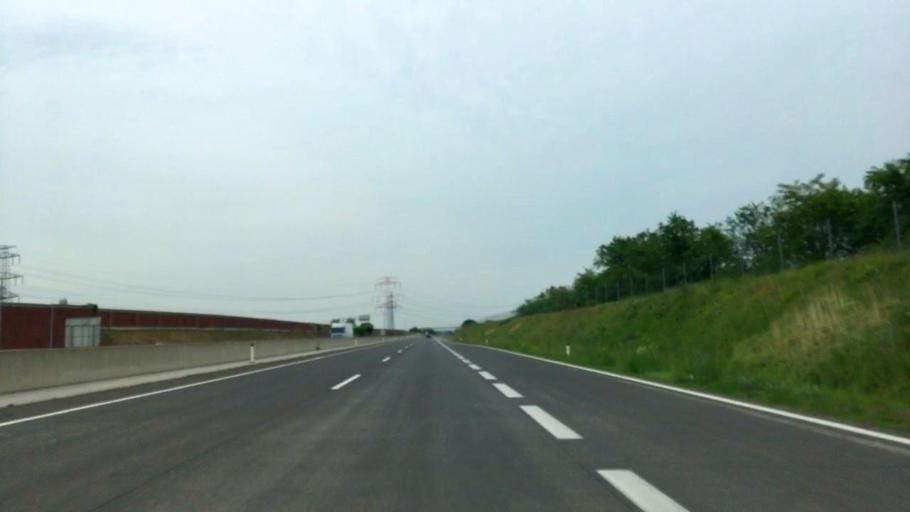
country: AT
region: Lower Austria
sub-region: Politischer Bezirk Korneuburg
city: Enzersfeld
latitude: 48.3456
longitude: 16.4406
